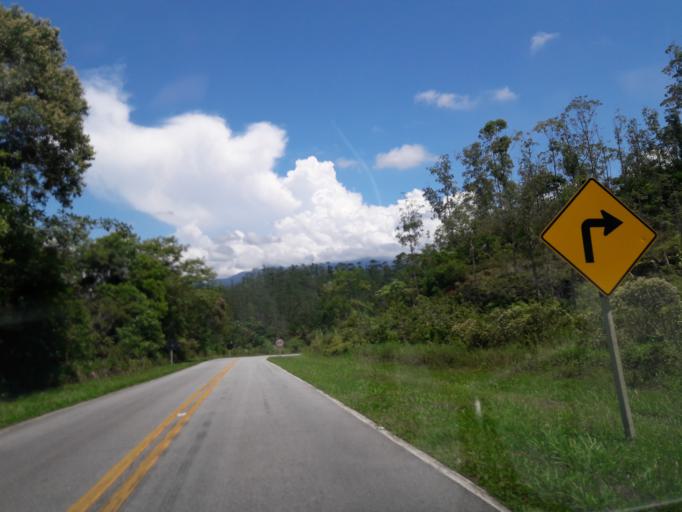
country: BR
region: Parana
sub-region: Antonina
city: Antonina
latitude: -25.5252
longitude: -48.7738
